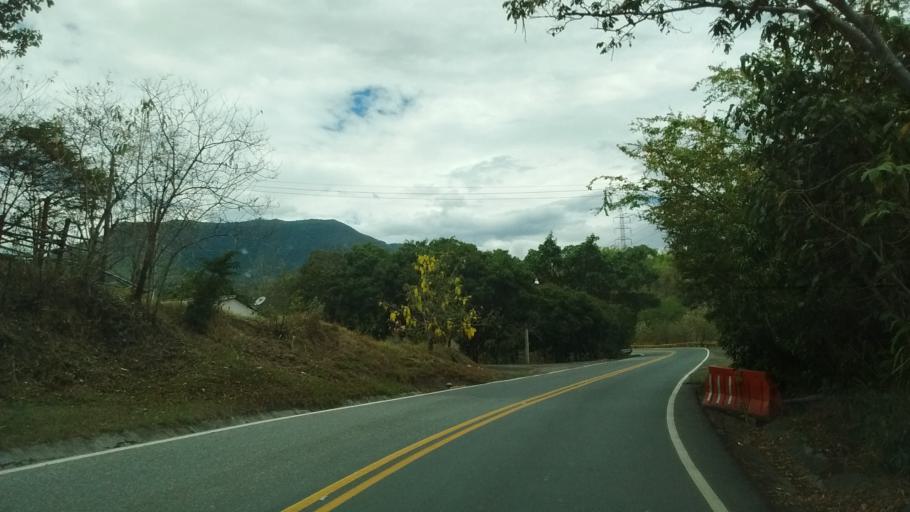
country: CO
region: Cauca
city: La Sierra
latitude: 2.2299
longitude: -76.7948
